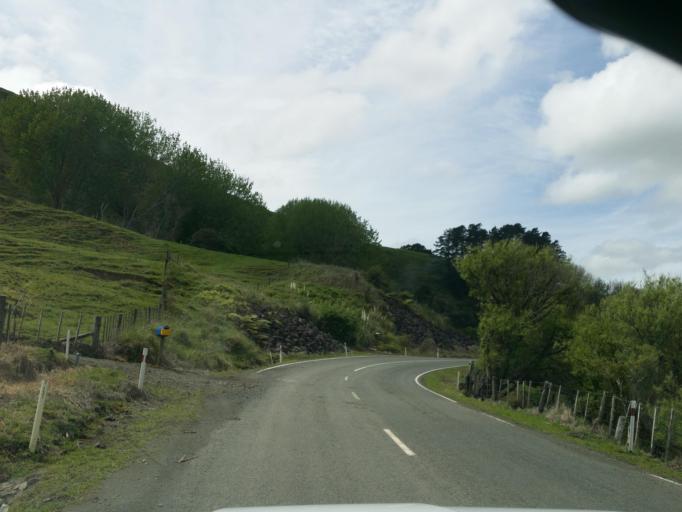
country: NZ
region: Northland
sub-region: Whangarei
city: Maungatapere
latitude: -35.8980
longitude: 174.0919
